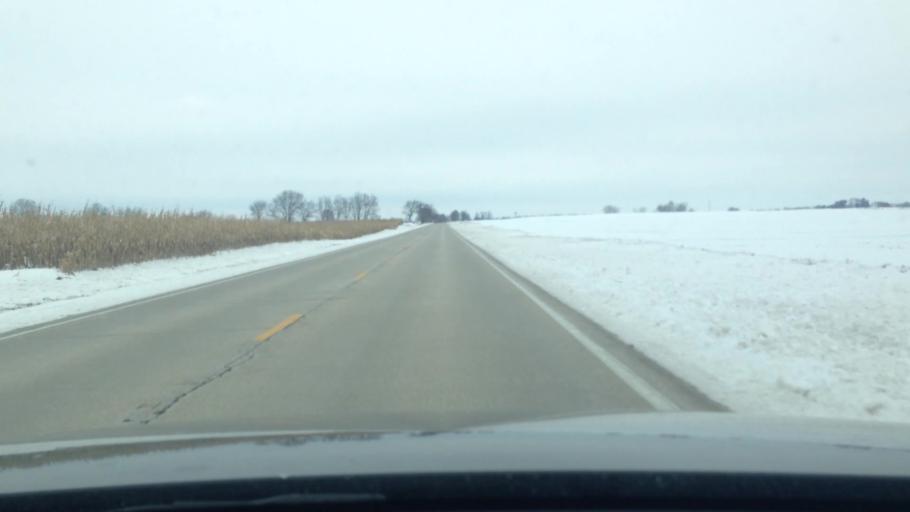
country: US
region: Illinois
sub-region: McHenry County
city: Hebron
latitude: 42.4292
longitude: -88.4381
